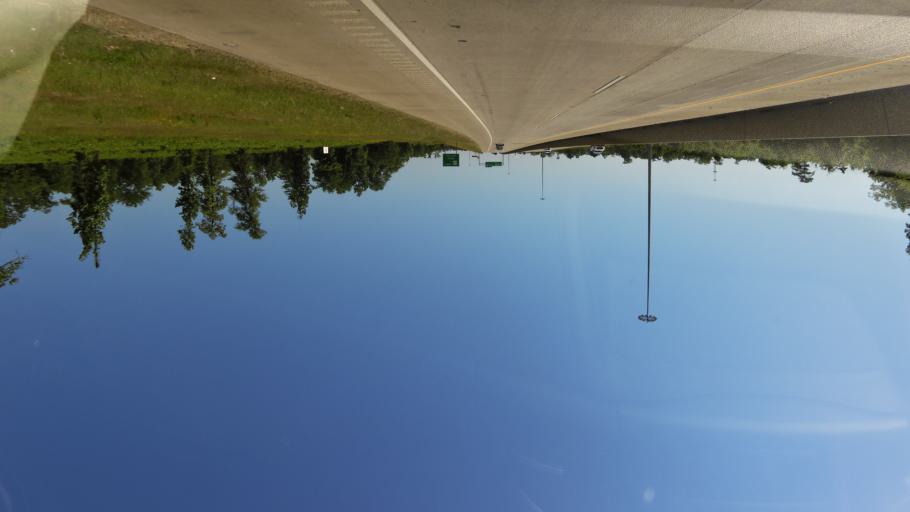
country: US
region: Texas
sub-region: Angelina County
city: Redland
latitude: 31.3792
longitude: -94.7116
